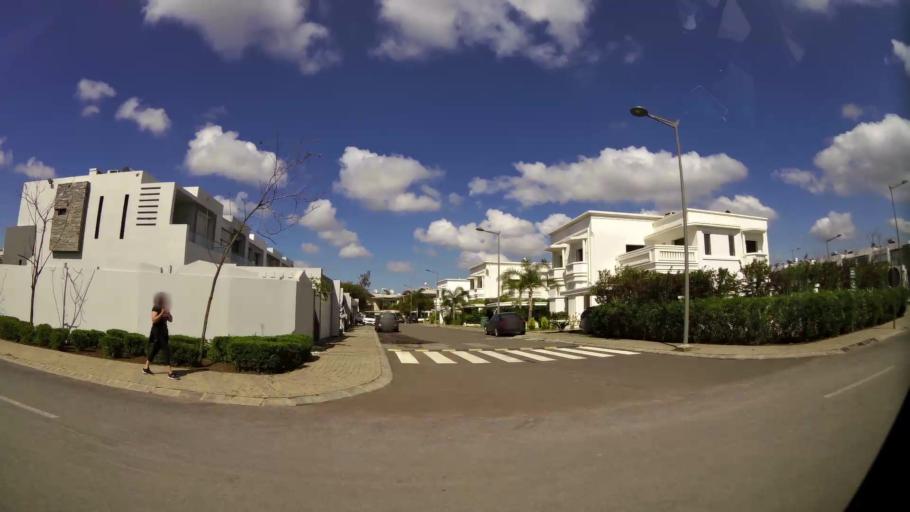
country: MA
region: Grand Casablanca
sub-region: Nouaceur
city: Bouskoura
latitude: 33.4679
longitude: -7.6031
